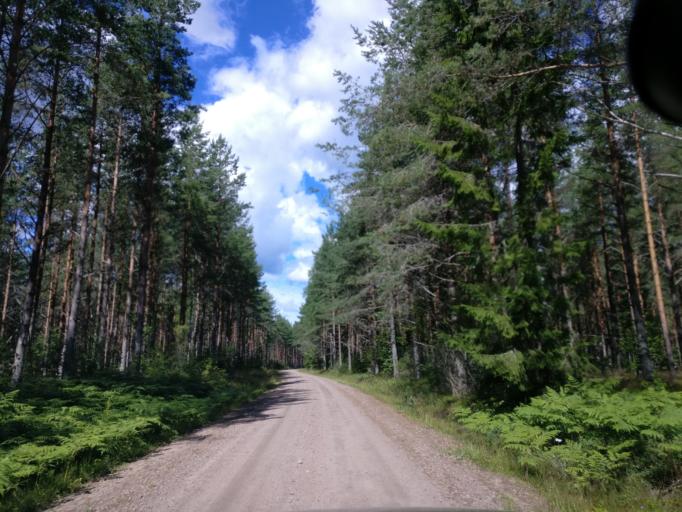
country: SE
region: Vaermland
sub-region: Hagfors Kommun
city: Hagfors
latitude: 60.0132
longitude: 13.5749
